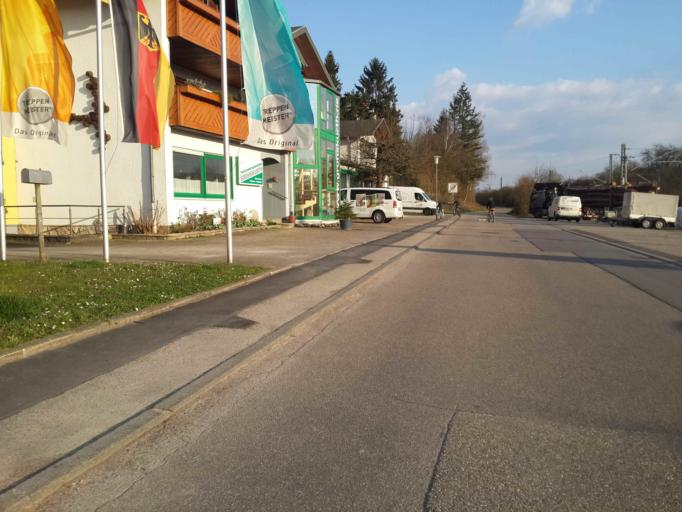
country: DE
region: Baden-Wuerttemberg
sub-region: Karlsruhe Region
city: Sinsheim
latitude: 49.2341
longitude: 8.9098
